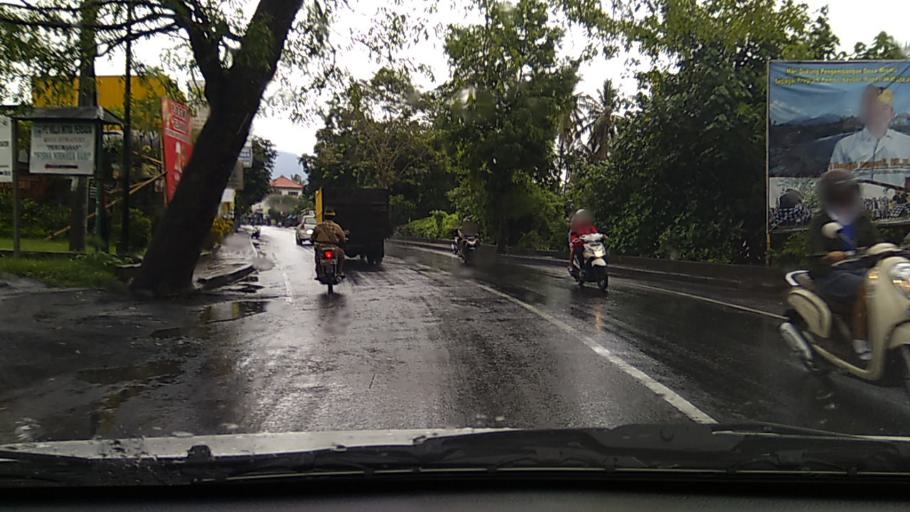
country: ID
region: Bali
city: Banjar Timbrah
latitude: -8.4758
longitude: 115.6167
